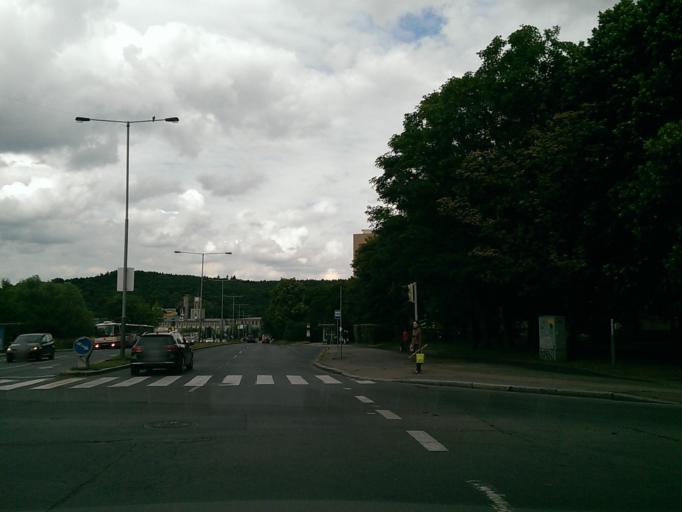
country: CZ
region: Praha
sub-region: Praha 4
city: Hodkovicky
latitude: 50.0280
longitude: 14.4512
